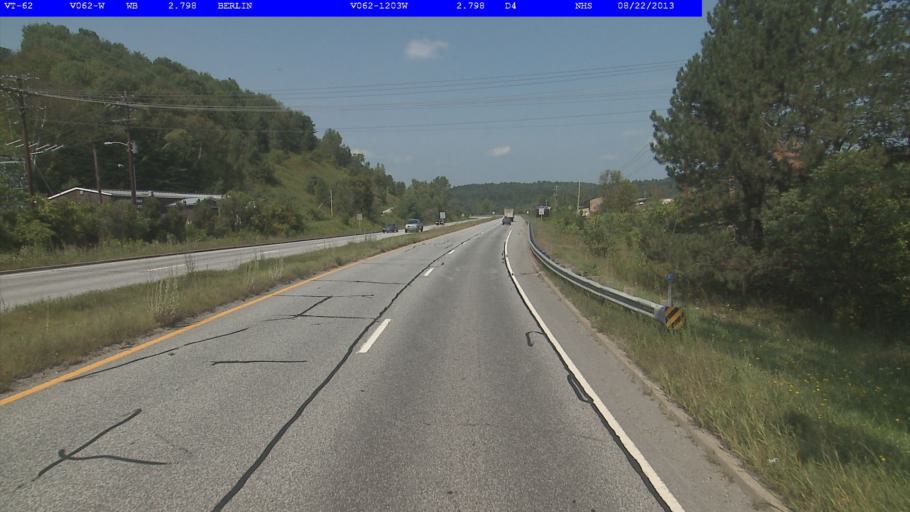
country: US
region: Vermont
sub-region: Washington County
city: Barre
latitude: 44.2056
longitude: -72.5174
